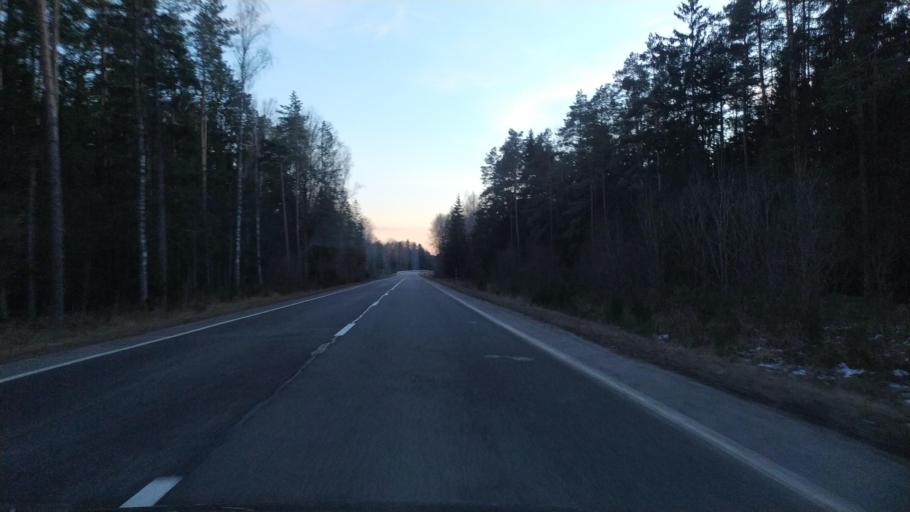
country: BY
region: Brest
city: Pruzhany
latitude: 52.5052
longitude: 24.1766
